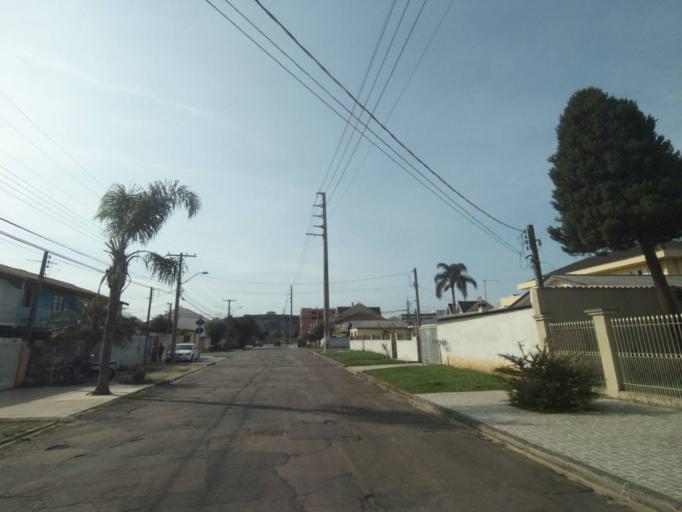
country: BR
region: Parana
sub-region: Curitiba
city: Curitiba
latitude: -25.4617
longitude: -49.3175
